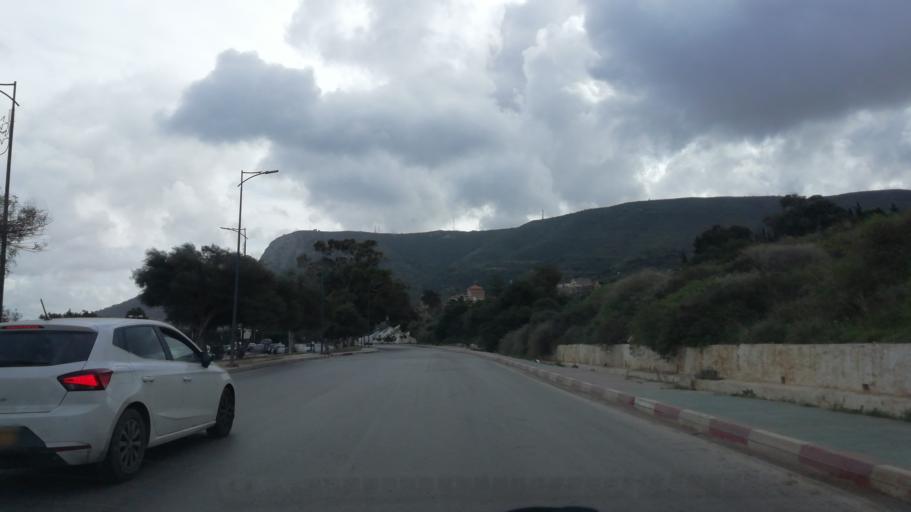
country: DZ
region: Oran
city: Mers el Kebir
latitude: 35.7177
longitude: -0.6977
